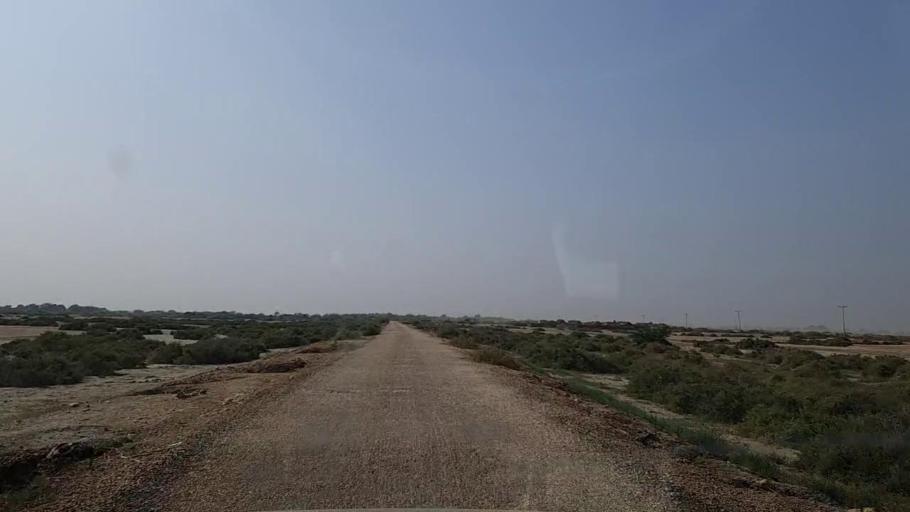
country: PK
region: Sindh
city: Mirpur Sakro
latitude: 24.5287
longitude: 67.5676
